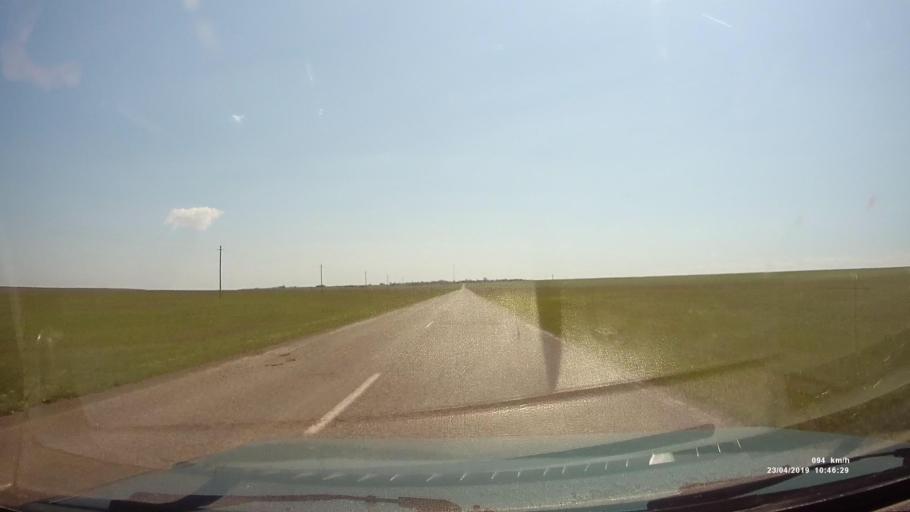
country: RU
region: Kalmykiya
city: Yashalta
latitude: 46.4426
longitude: 42.6919
